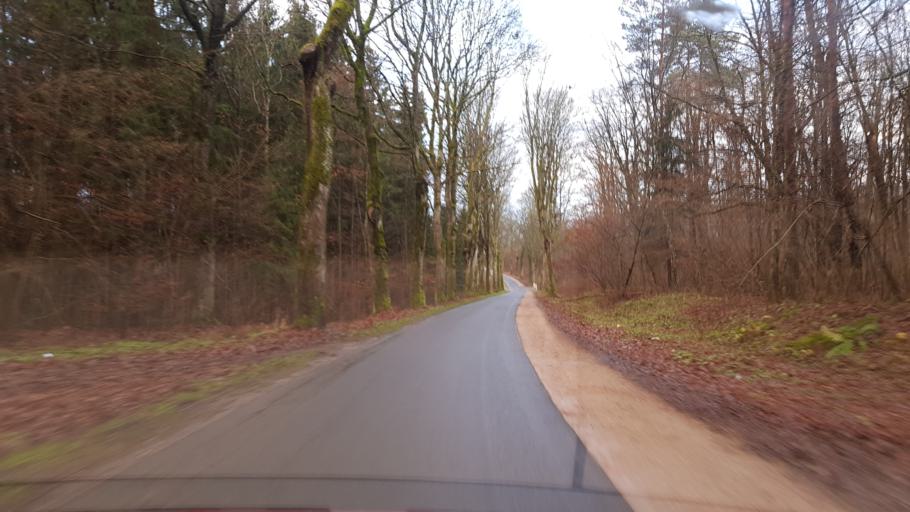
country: PL
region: West Pomeranian Voivodeship
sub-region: Powiat bialogardzki
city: Karlino
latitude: 53.9523
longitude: 15.9033
